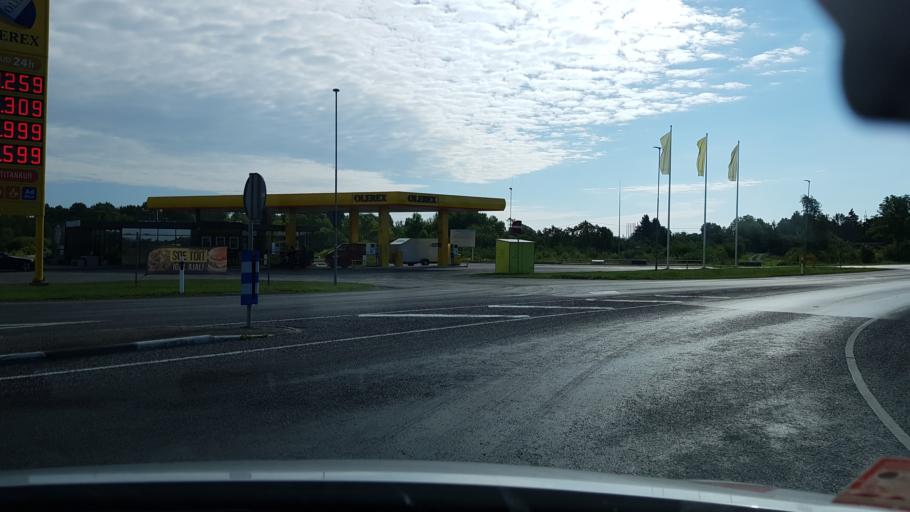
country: EE
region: Laeaene
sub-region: Lihula vald
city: Lihula
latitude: 58.6845
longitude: 23.8098
